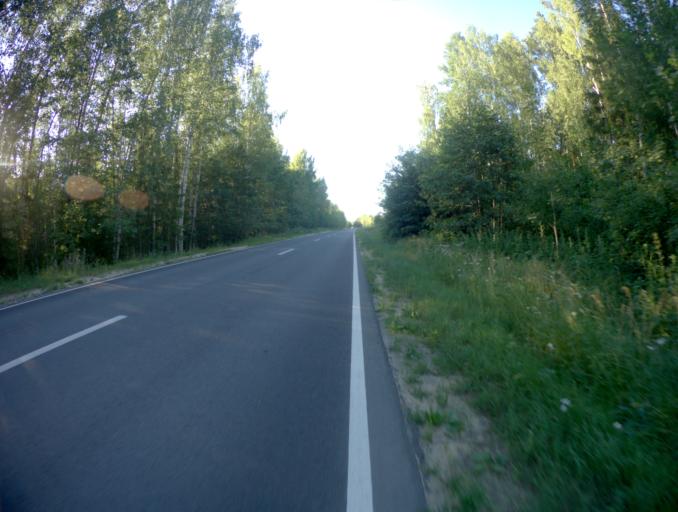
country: RU
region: Vladimir
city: Galitsy
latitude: 56.1226
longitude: 42.8730
